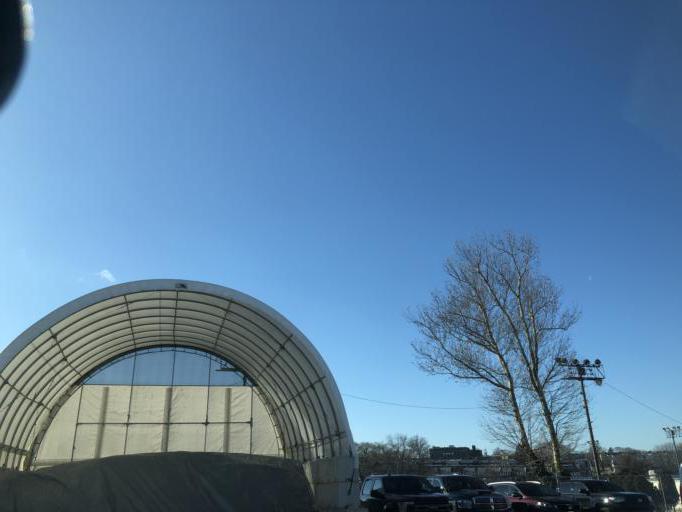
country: US
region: Pennsylvania
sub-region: Delaware County
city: East Lansdowne
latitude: 39.9526
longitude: -75.2539
